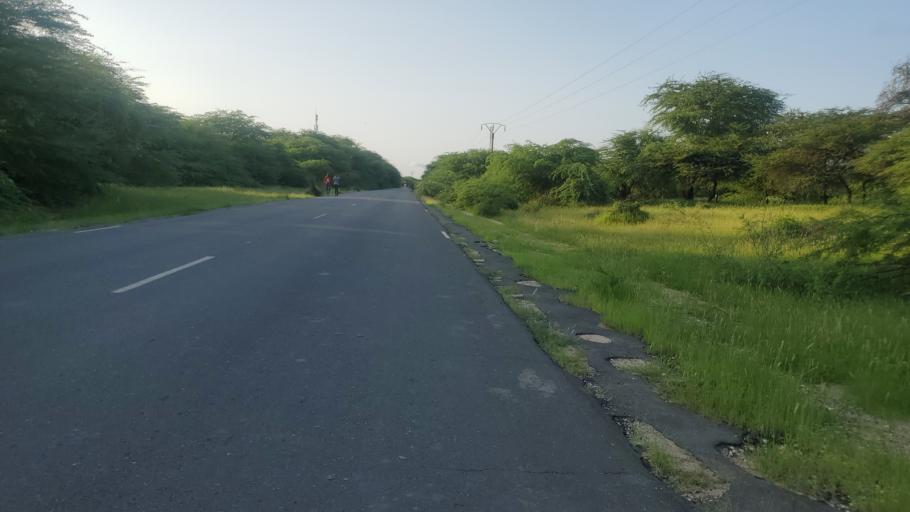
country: SN
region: Saint-Louis
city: Saint-Louis
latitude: 16.2018
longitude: -16.4125
